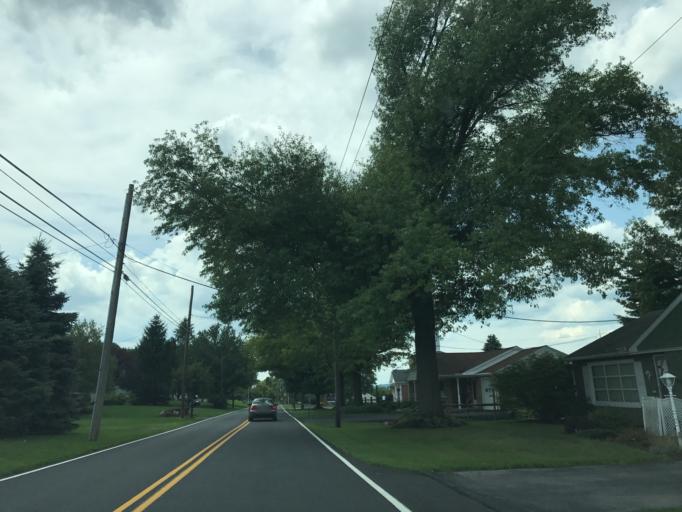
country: US
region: Pennsylvania
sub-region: Lancaster County
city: Penryn
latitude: 40.2077
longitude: -76.3792
